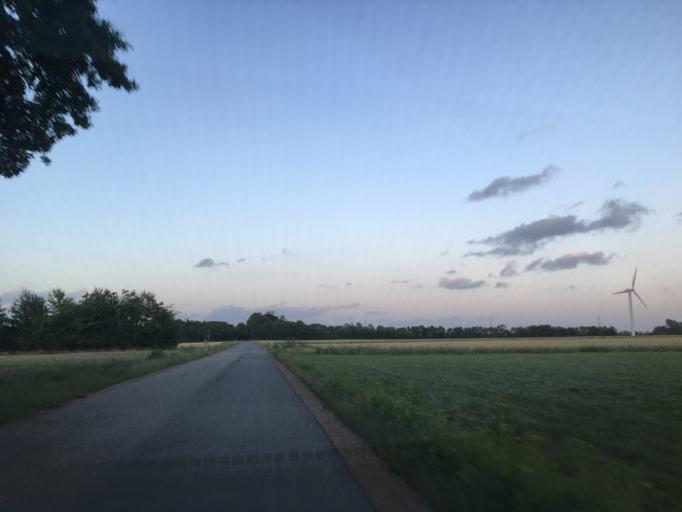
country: DK
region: Zealand
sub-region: Solrod Kommune
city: Havdrup
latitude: 55.5223
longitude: 12.0994
